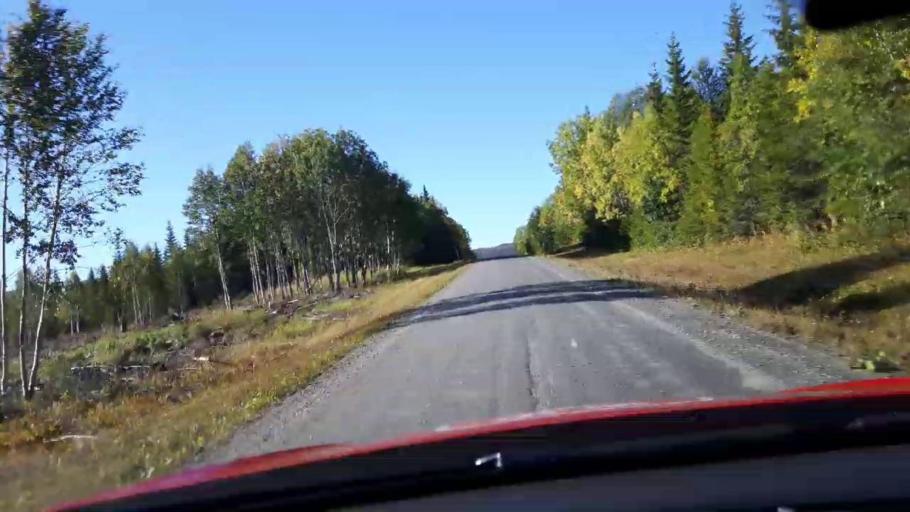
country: NO
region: Nord-Trondelag
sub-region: Lierne
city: Sandvika
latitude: 64.5903
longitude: 13.8478
